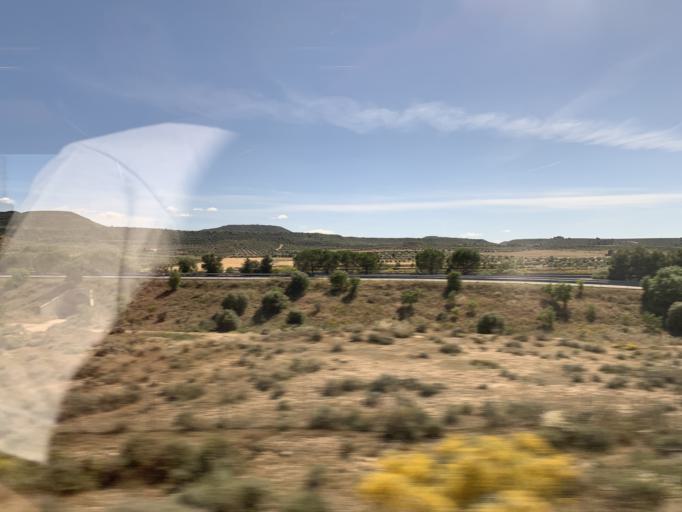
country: ES
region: Catalonia
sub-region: Provincia de Lleida
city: Juneda
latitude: 41.5049
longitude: 0.8457
